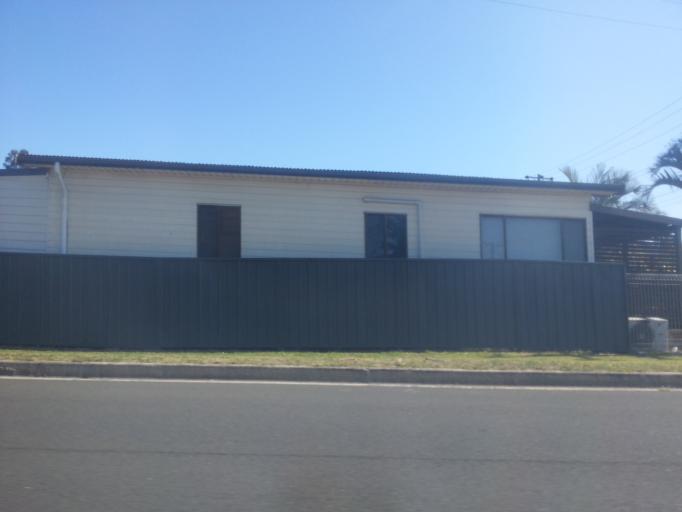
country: AU
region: New South Wales
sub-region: Wollongong
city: Corrimal
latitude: -34.3872
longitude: 150.9061
